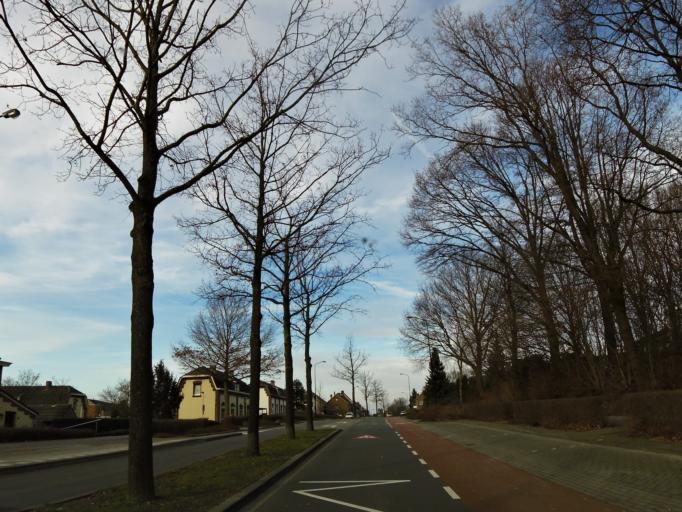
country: NL
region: Limburg
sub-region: Gemeente Heerlen
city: Heerlen
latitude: 50.9070
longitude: 5.9660
